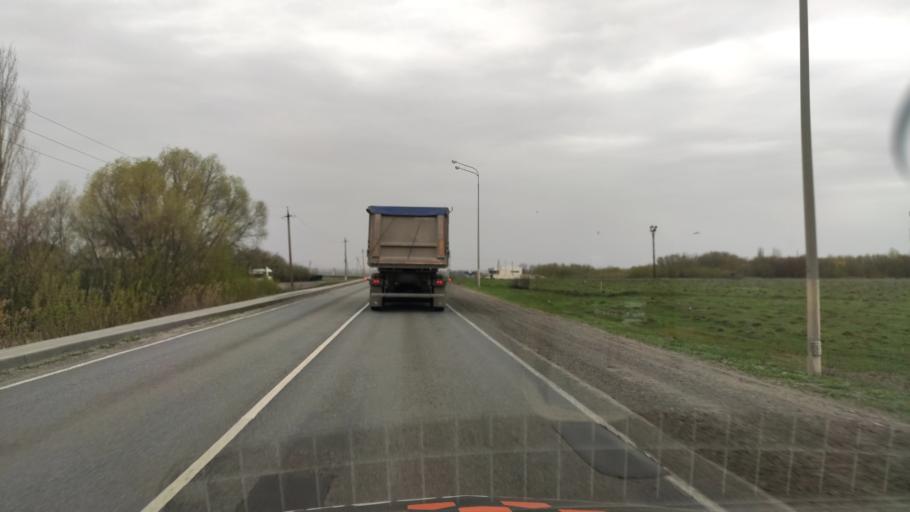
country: RU
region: Kursk
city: Gorshechnoye
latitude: 51.5302
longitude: 38.0226
